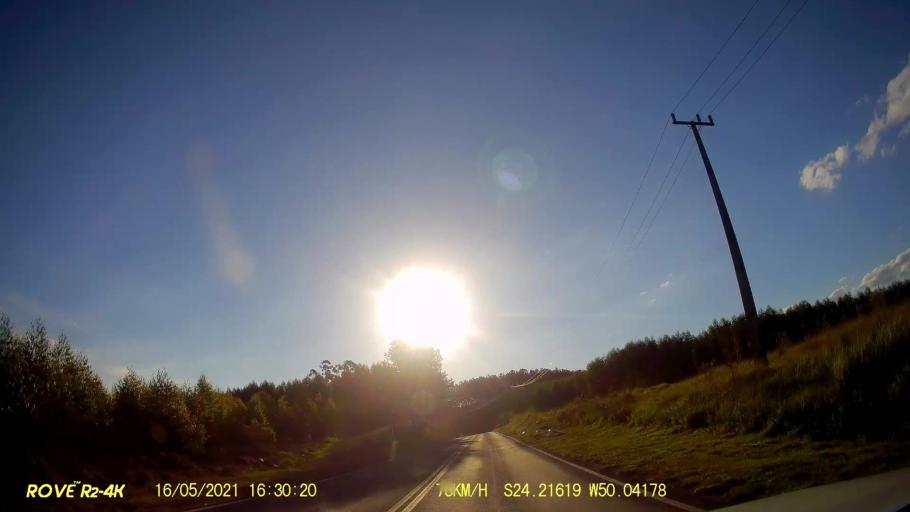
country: BR
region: Parana
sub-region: Pirai Do Sul
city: Pirai do Sul
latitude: -24.2164
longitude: -50.0419
